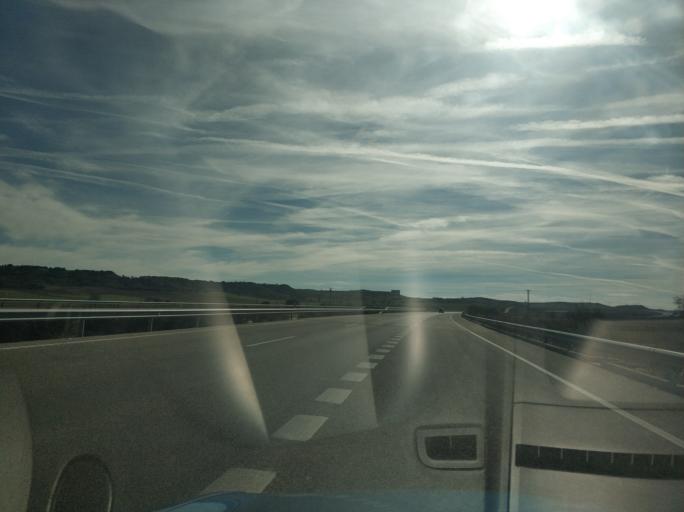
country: ES
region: Castille and Leon
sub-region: Provincia de Zamora
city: Corrales
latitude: 41.3567
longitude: -5.7135
